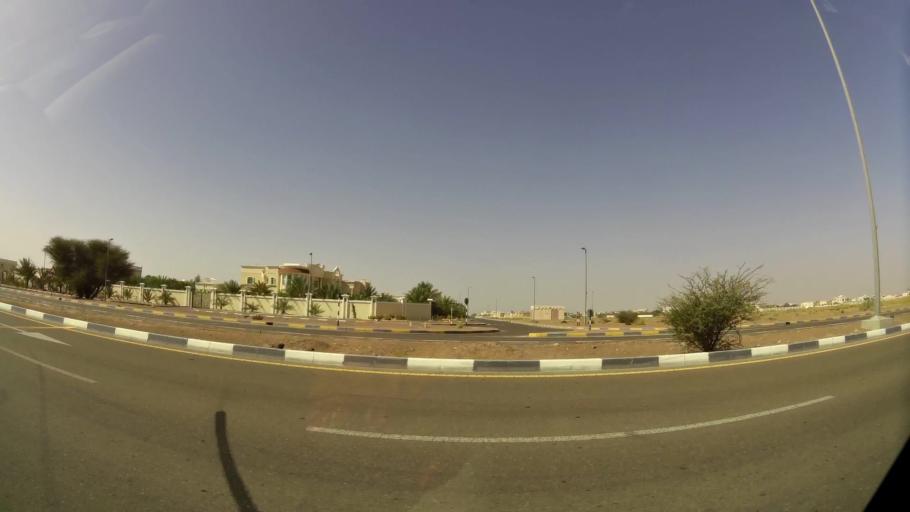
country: OM
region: Al Buraimi
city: Al Buraymi
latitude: 24.3436
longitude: 55.7916
